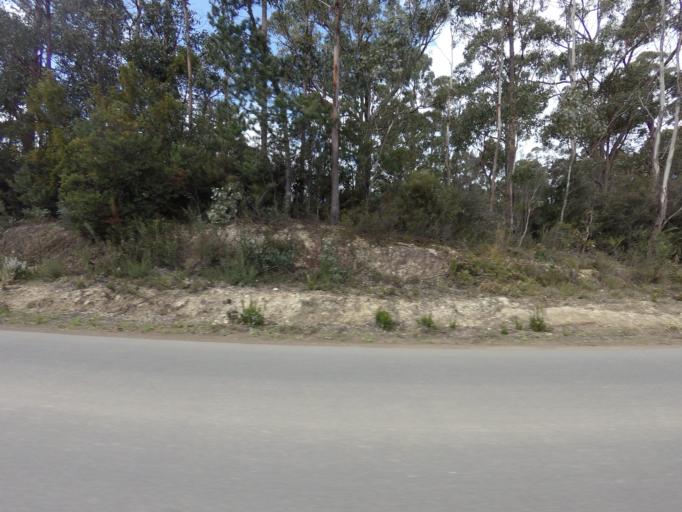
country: AU
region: Tasmania
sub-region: Huon Valley
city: Geeveston
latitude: -43.3313
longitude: 146.9708
